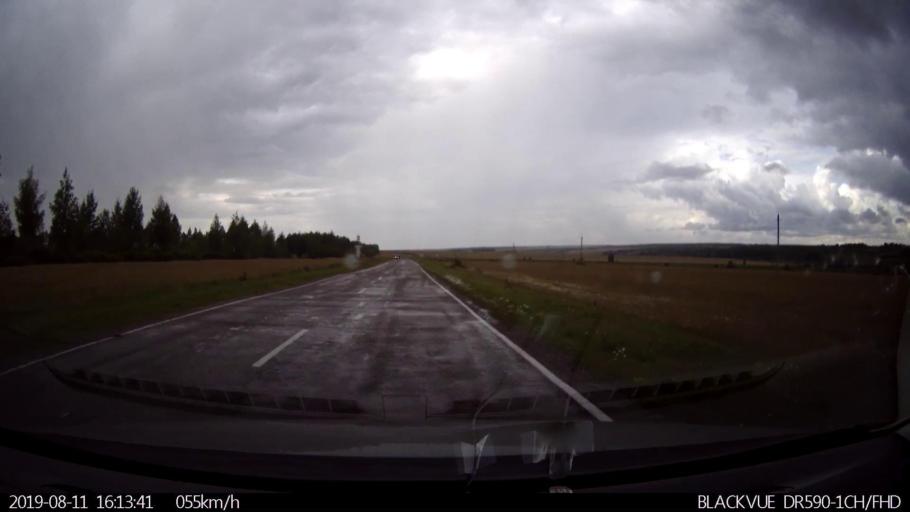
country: RU
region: Ulyanovsk
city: Ignatovka
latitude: 54.0221
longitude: 47.6361
